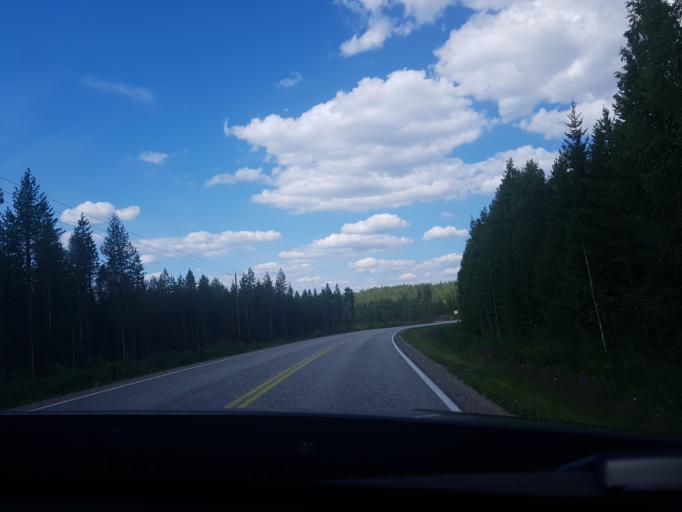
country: FI
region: Kainuu
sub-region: Kehys-Kainuu
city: Kuhmo
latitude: 64.2454
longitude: 29.8073
